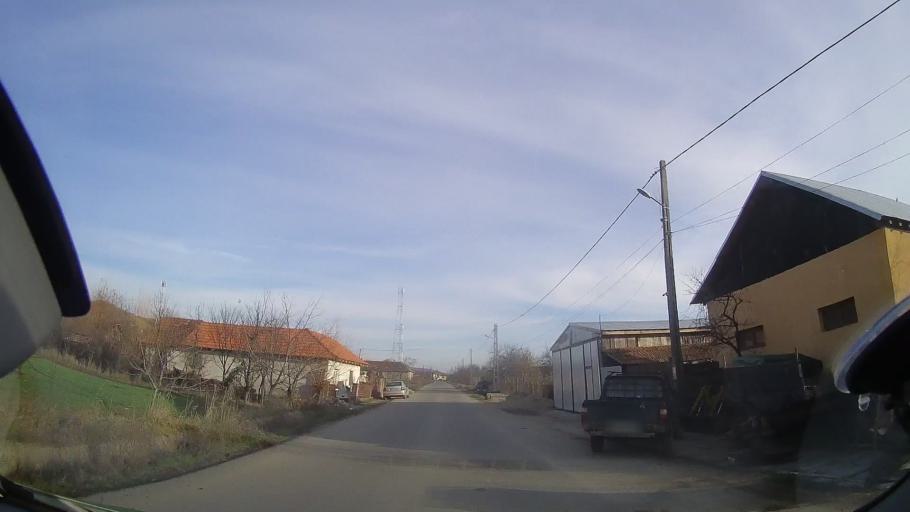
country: RO
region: Bihor
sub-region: Comuna Tileagd
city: Tileagd
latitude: 47.0824
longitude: 22.1975
